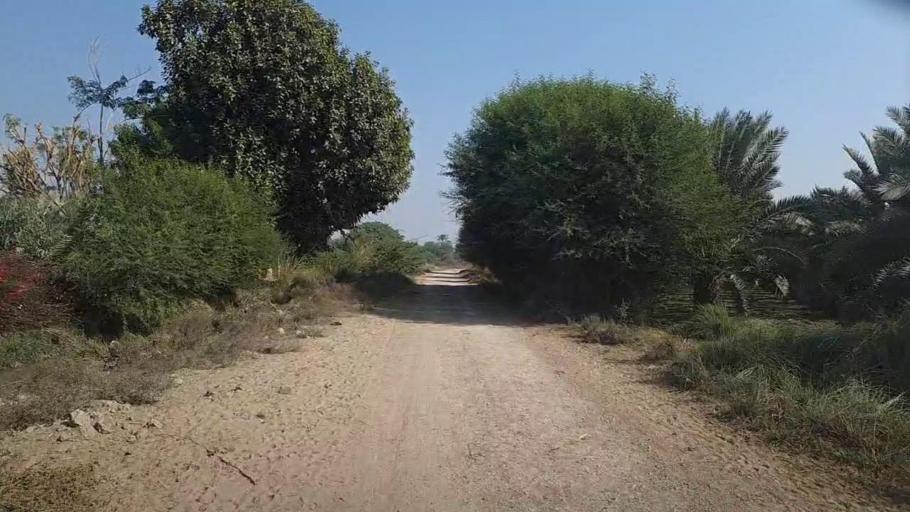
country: PK
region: Sindh
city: Bozdar
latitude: 27.1915
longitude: 68.6161
